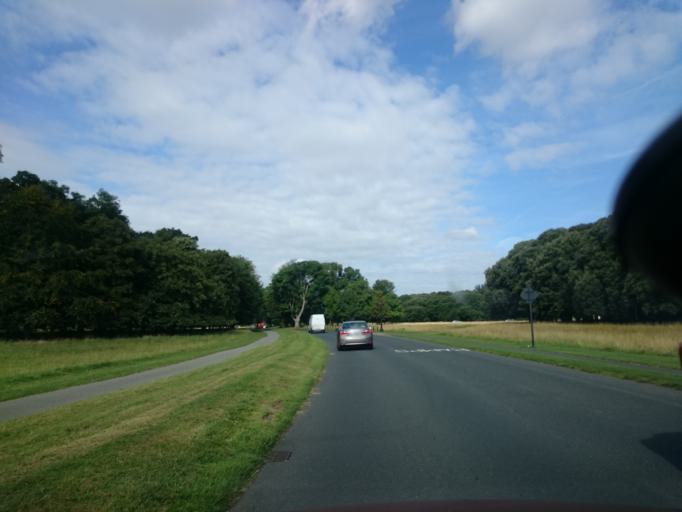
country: IE
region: Leinster
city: Chapelizod
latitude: 53.3690
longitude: -6.3312
